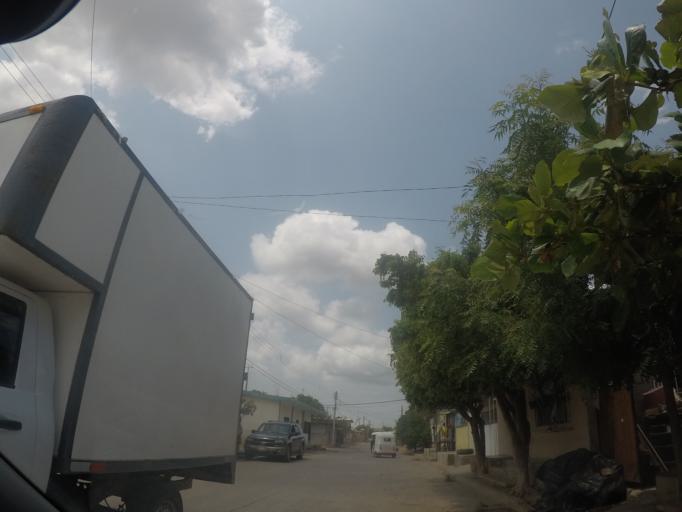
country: MX
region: Oaxaca
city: El Espinal
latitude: 16.5516
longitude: -94.9462
